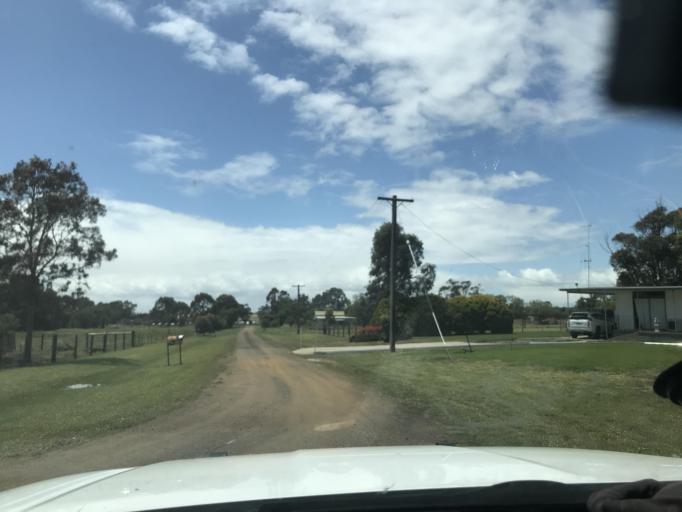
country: AU
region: South Australia
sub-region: Tatiara
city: Bordertown
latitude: -36.3632
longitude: 141.1264
